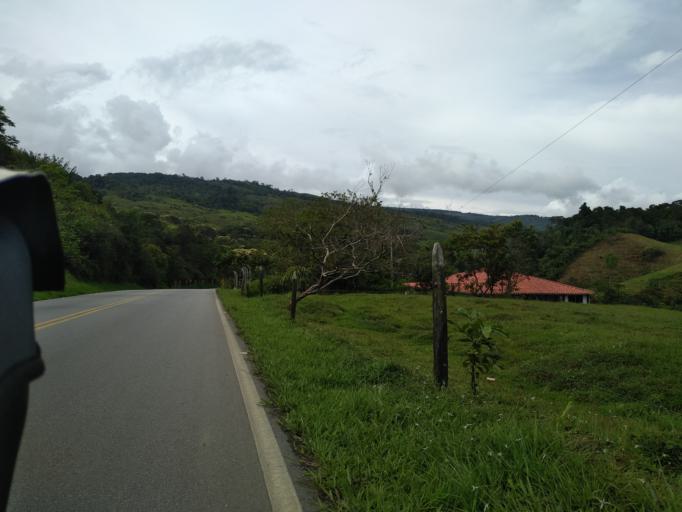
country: CO
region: Santander
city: Suaita
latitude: 6.1113
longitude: -73.3671
